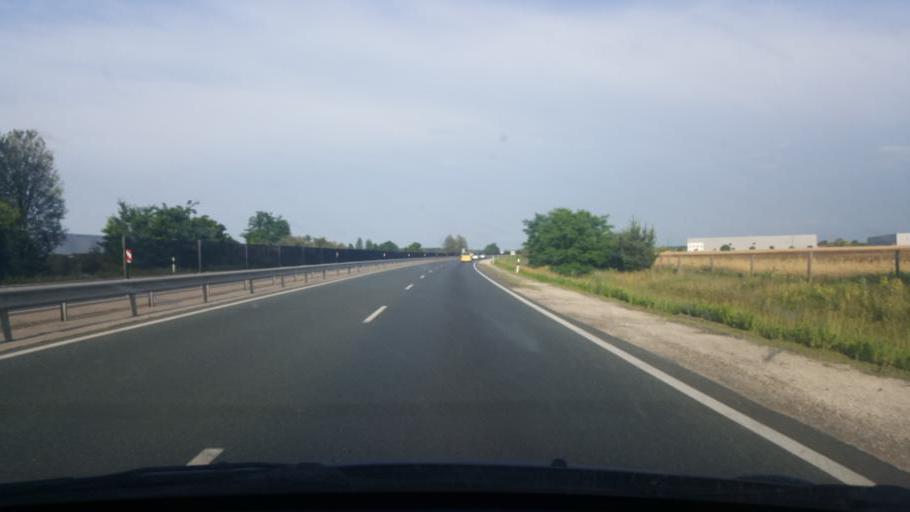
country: HU
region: Pest
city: Ullo
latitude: 47.4032
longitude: 19.3461
